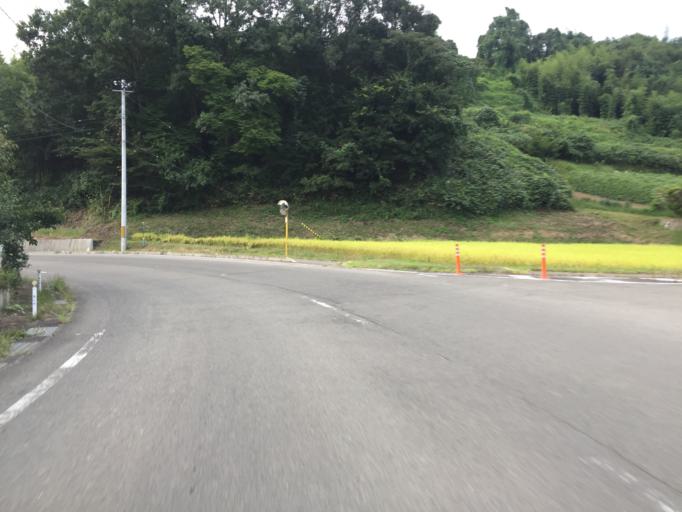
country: JP
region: Fukushima
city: Hobaramachi
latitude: 37.7794
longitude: 140.6028
